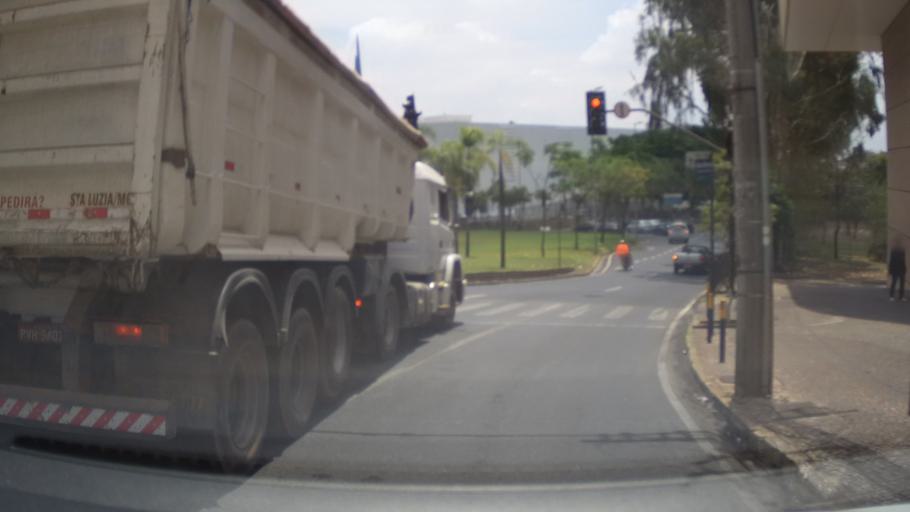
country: BR
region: Minas Gerais
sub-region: Belo Horizonte
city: Belo Horizonte
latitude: -19.9747
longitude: -43.9423
